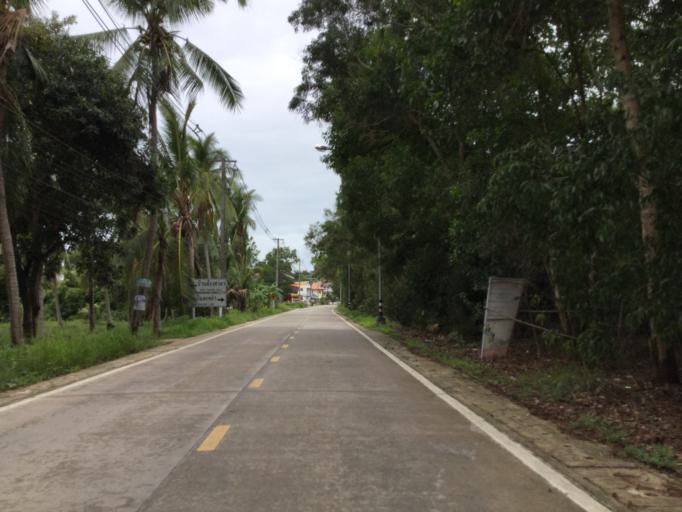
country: TH
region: Surat Thani
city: Ko Pha-Ngan
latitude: 9.7186
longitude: 99.9986
